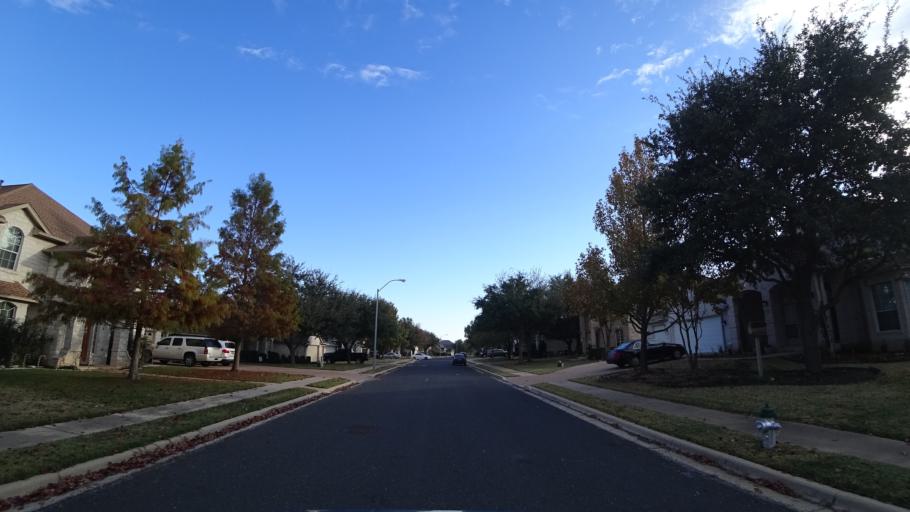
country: US
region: Texas
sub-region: Williamson County
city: Brushy Creek
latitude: 30.5033
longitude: -97.7374
